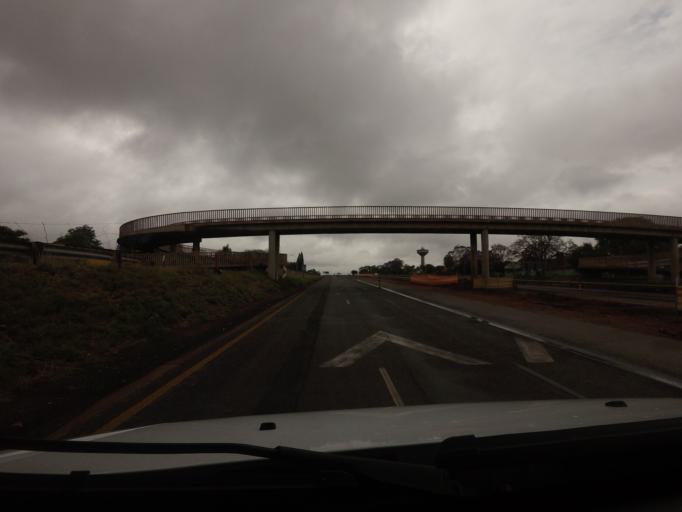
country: ZA
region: Mpumalanga
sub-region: Nkangala District Municipality
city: Witbank
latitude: -25.8872
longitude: 29.2238
